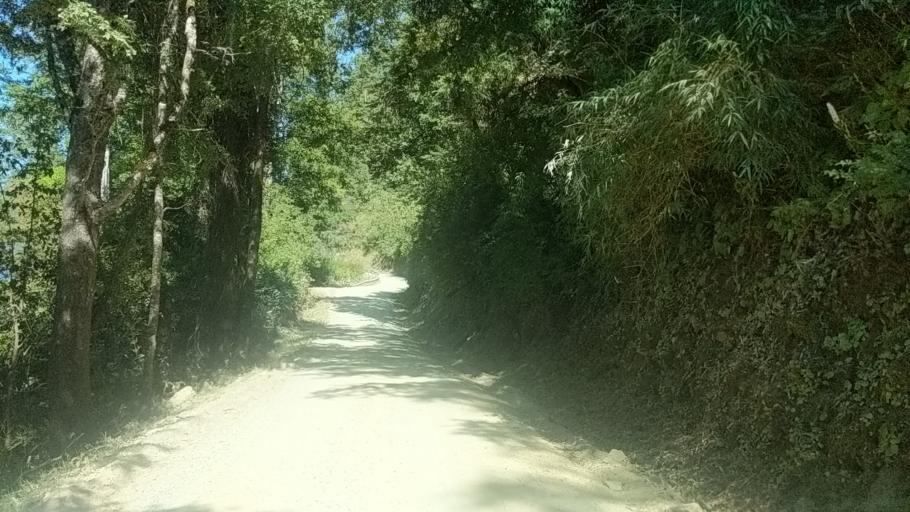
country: CL
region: Araucania
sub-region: Provincia de Cautin
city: Pucon
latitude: -39.0626
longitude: -71.7092
